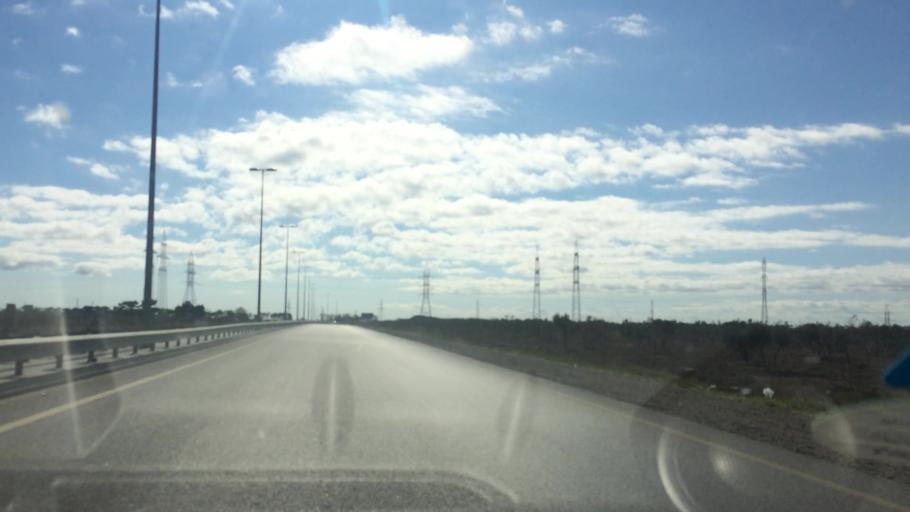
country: AZ
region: Baki
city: Qala
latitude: 40.4396
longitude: 50.1820
